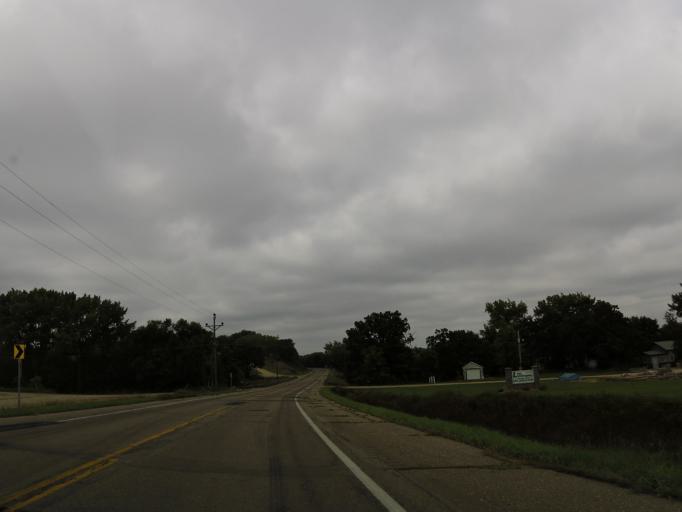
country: US
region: Minnesota
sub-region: Yellow Medicine County
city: Granite Falls
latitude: 44.8593
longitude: -95.6310
